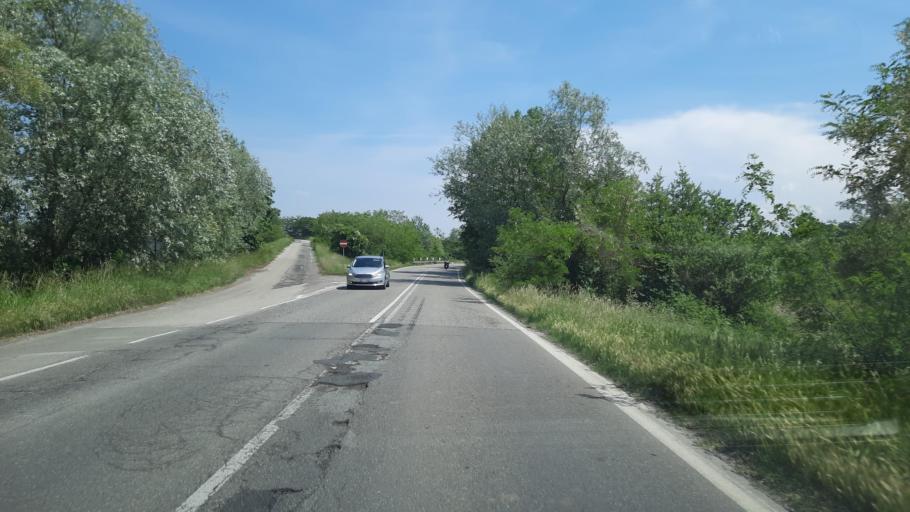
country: IT
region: Lombardy
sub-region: Provincia di Pavia
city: Tromello
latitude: 45.2170
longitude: 8.8537
